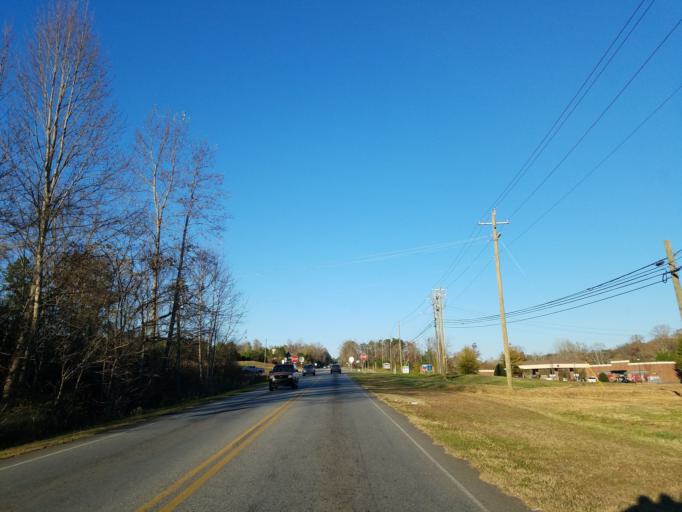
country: US
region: Georgia
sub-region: Cherokee County
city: Ball Ground
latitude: 34.3260
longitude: -84.3903
